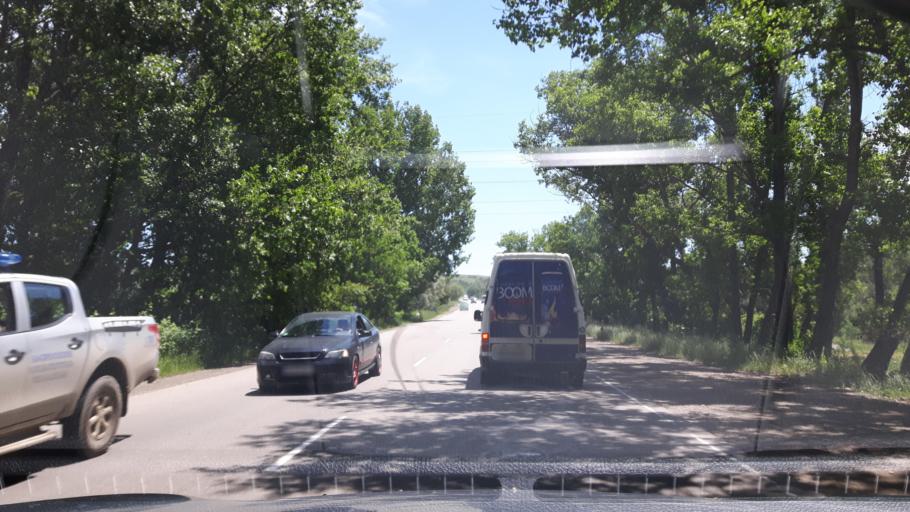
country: GE
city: Didi Lilo
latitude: 41.6943
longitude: 45.0601
